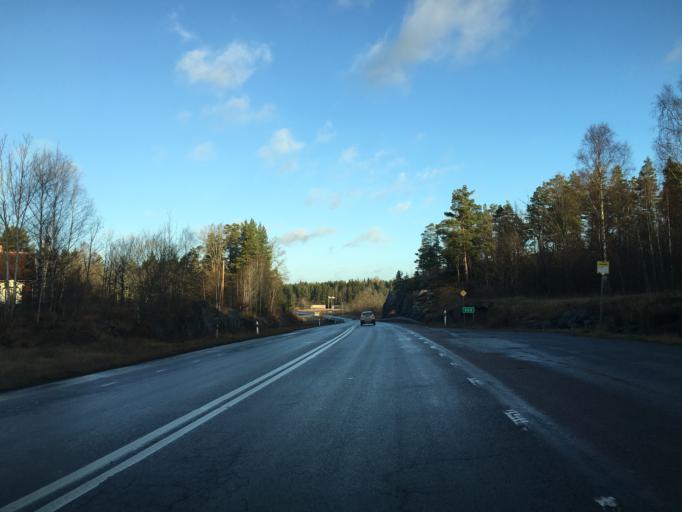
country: SE
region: Kalmar
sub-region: Vasterviks Kommun
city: Ankarsrum
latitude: 57.6575
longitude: 16.4442
